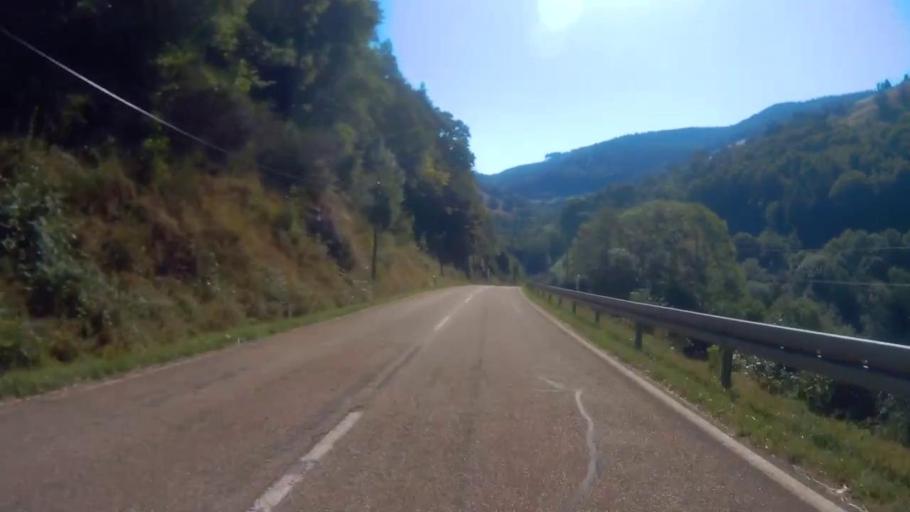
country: DE
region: Baden-Wuerttemberg
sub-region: Freiburg Region
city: Tunau
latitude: 47.7621
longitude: 7.9183
